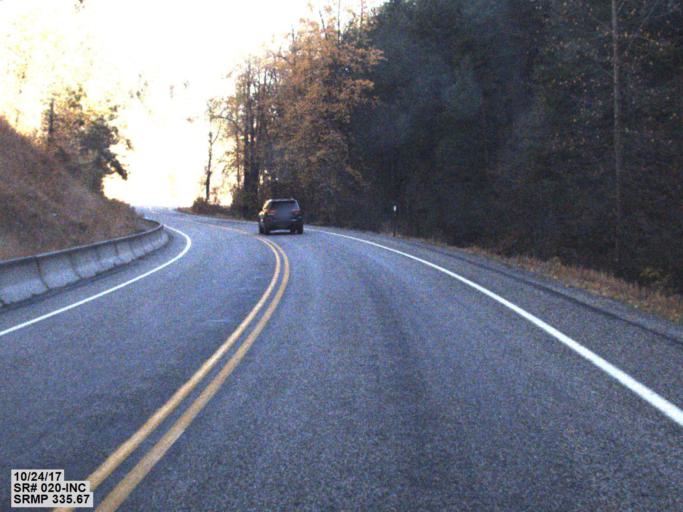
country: US
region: Washington
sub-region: Stevens County
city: Kettle Falls
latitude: 48.5843
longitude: -118.2140
